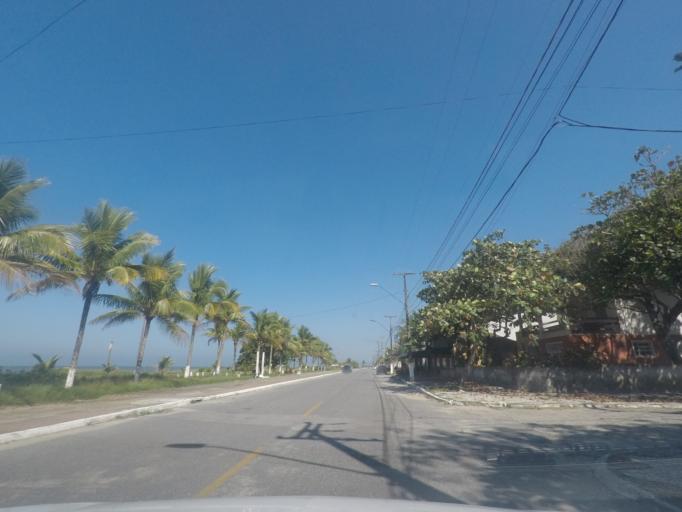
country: BR
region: Parana
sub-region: Pontal Do Parana
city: Pontal do Parana
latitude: -25.7234
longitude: -48.4843
